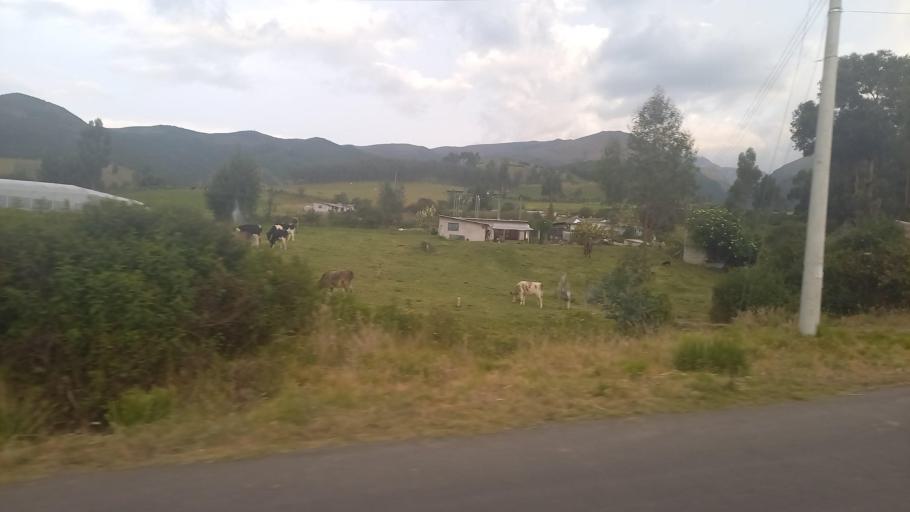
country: EC
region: Pichincha
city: Cayambe
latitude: 0.0942
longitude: -78.0905
